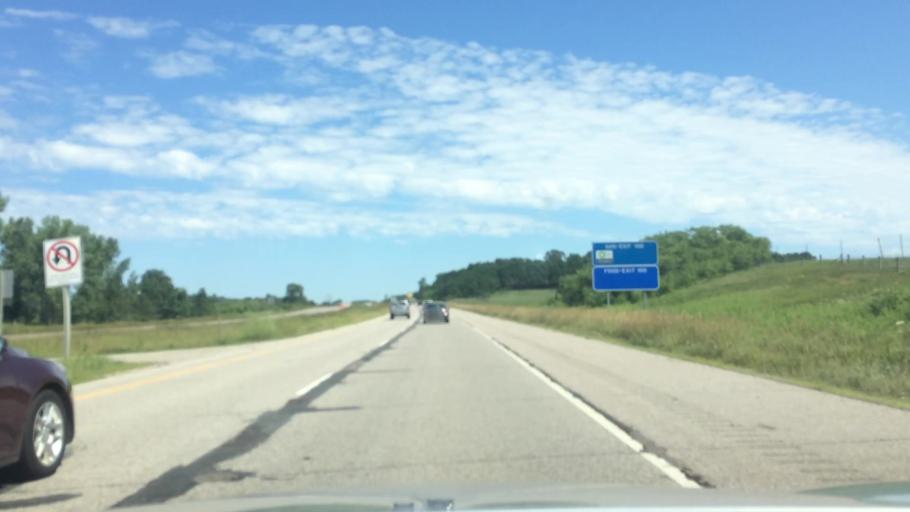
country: US
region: Wisconsin
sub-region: Columbia County
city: Portage
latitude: 43.6917
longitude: -89.4697
